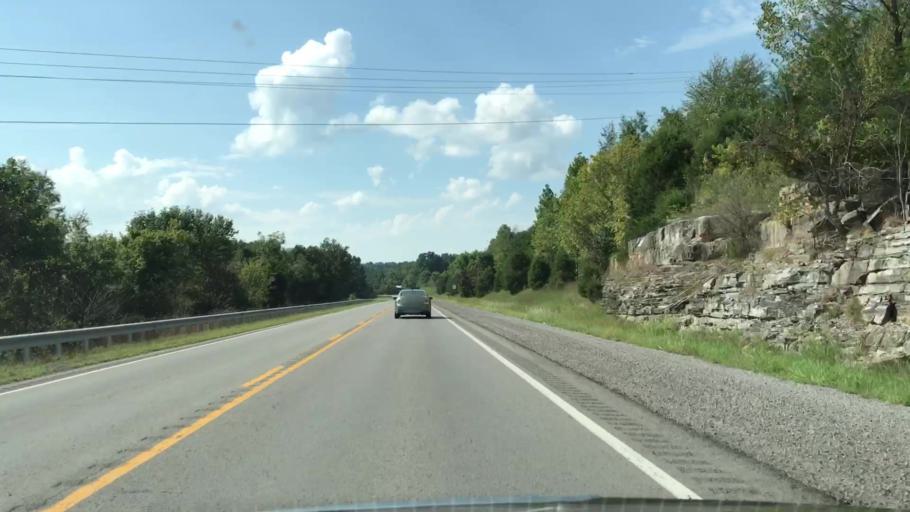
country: US
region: Kentucky
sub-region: Allen County
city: Scottsville
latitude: 36.6904
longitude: -86.2529
